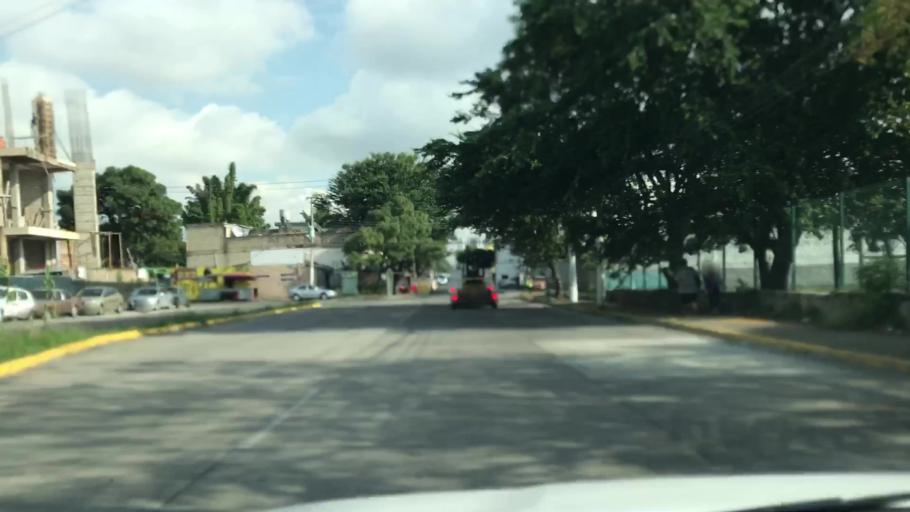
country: MX
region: Jalisco
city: Guadalajara
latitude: 20.6432
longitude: -103.4329
